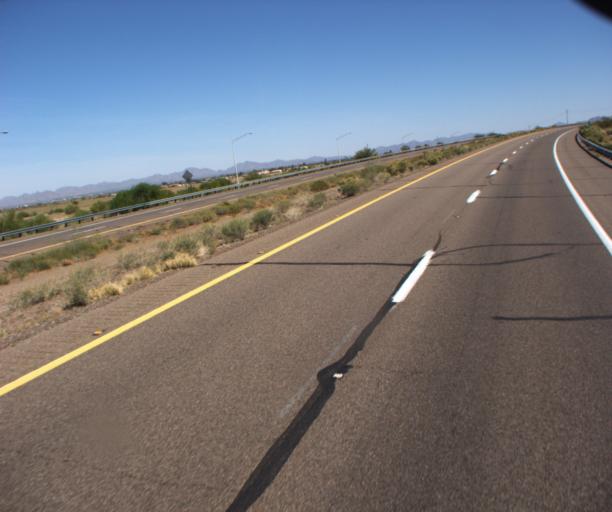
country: US
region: Arizona
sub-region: Maricopa County
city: Gila Bend
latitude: 32.9429
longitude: -112.7459
